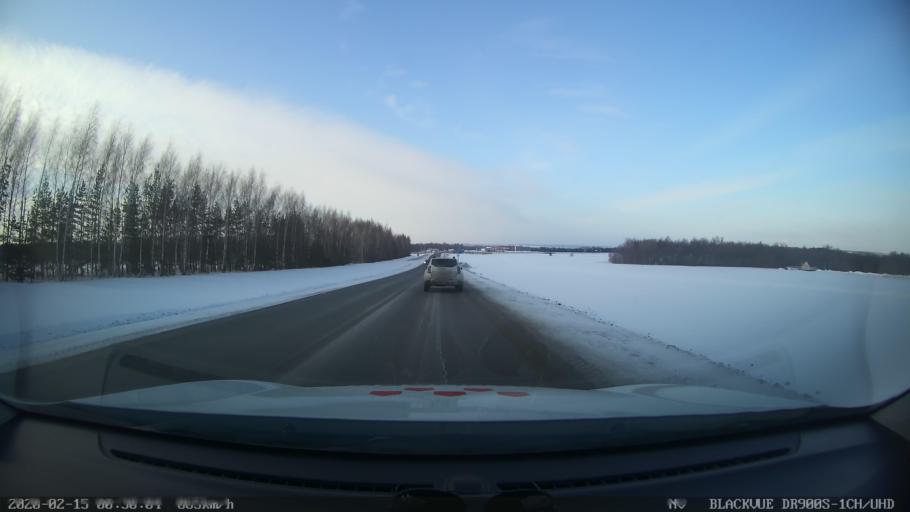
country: RU
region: Tatarstan
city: Verkhniy Uslon
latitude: 55.6562
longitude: 48.8614
